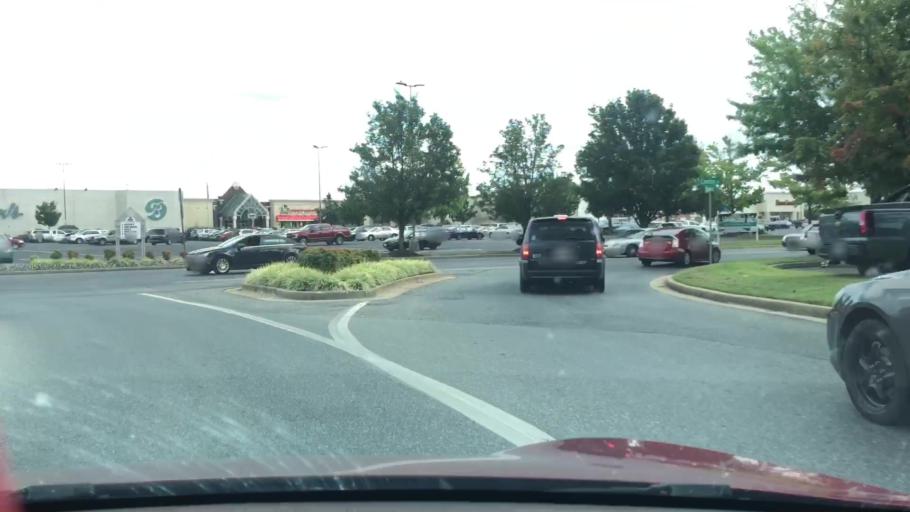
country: US
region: Maryland
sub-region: Wicomico County
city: Salisbury
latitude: 38.4012
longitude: -75.5687
